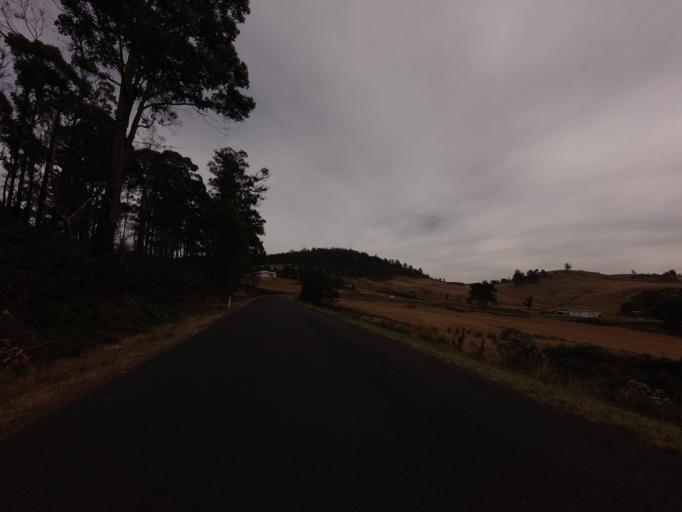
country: AU
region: Tasmania
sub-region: Sorell
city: Sorell
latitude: -42.4886
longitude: 147.5652
